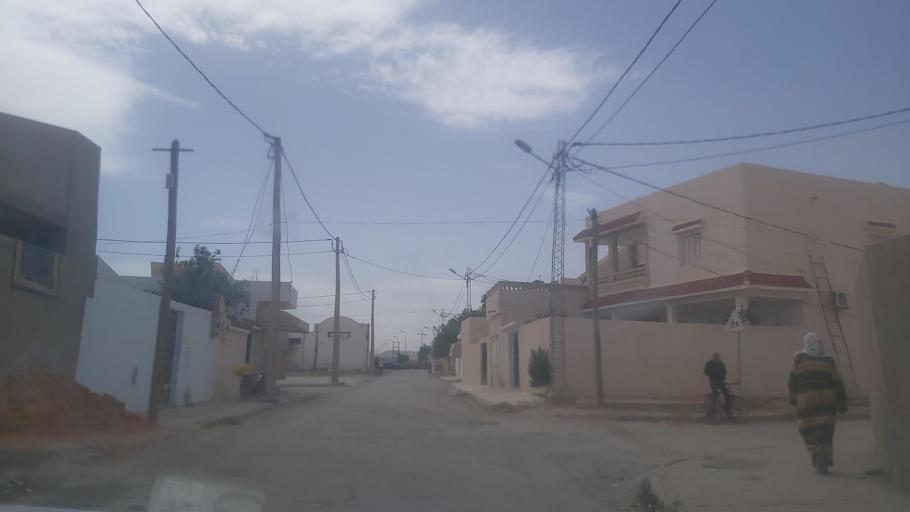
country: TN
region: Silyanah
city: Bu `Aradah
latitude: 36.3524
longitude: 9.6299
